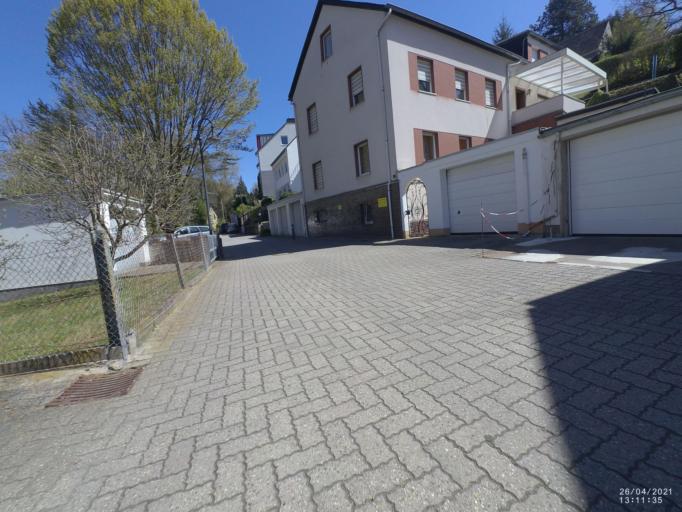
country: DE
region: Rheinland-Pfalz
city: Vallendar
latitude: 50.4022
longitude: 7.6228
